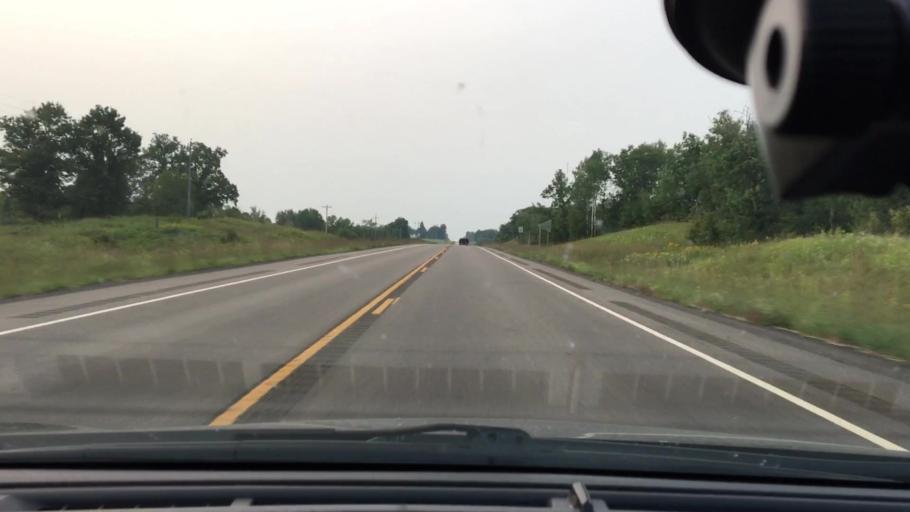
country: US
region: Minnesota
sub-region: Crow Wing County
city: Crosby
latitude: 46.5546
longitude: -93.9527
